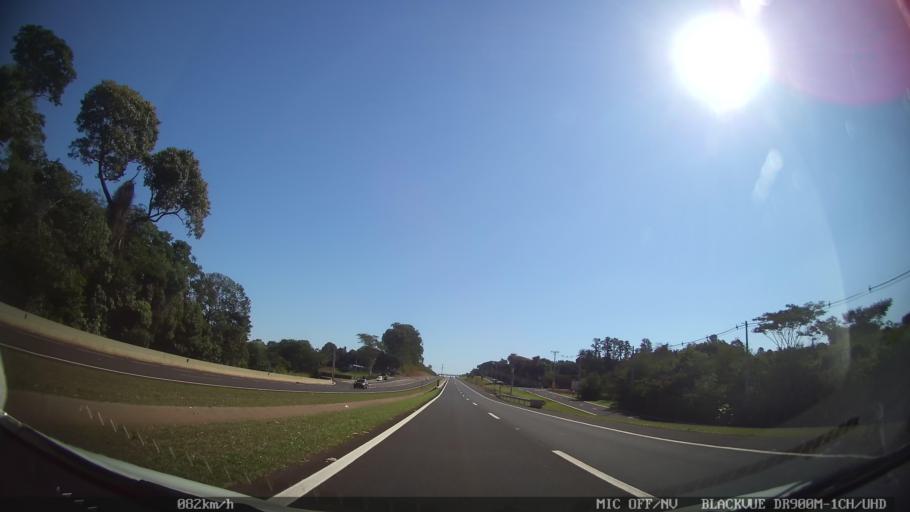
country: BR
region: Sao Paulo
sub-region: Ribeirao Preto
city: Ribeirao Preto
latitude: -21.2120
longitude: -47.8450
